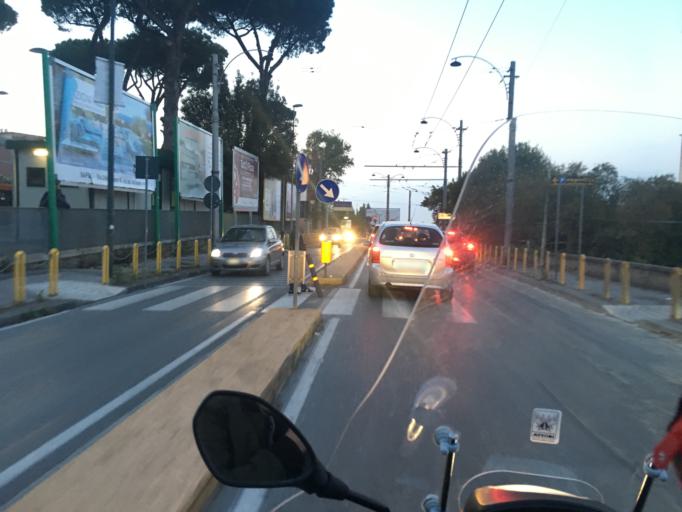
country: IT
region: Campania
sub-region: Provincia di Napoli
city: Napoli
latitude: 40.8678
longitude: 14.2276
